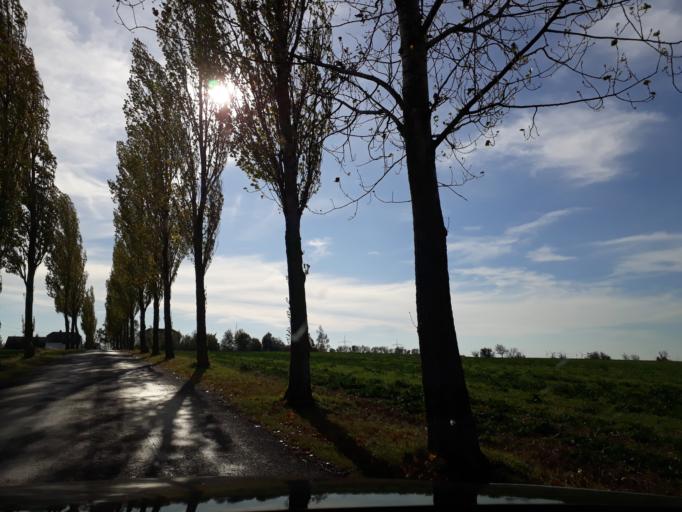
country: DE
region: Saxony
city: Niederstriegis
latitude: 51.1034
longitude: 13.1557
